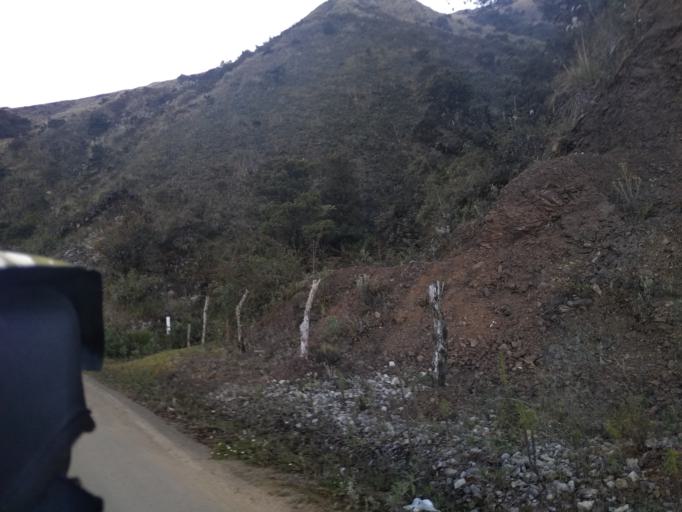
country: PE
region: Amazonas
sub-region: Provincia de Chachapoyas
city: Montevideo
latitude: -6.7213
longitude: -77.8766
